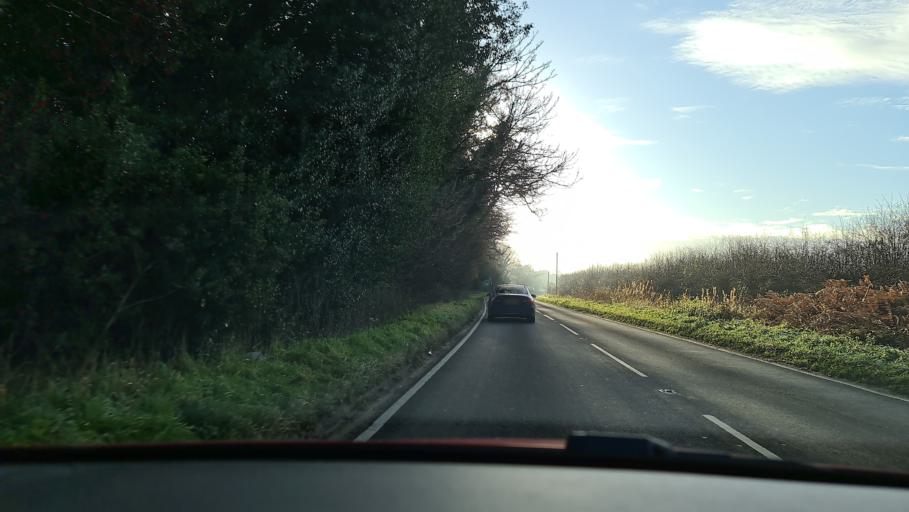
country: GB
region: England
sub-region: Buckinghamshire
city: Great Missenden
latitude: 51.7194
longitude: -0.7189
